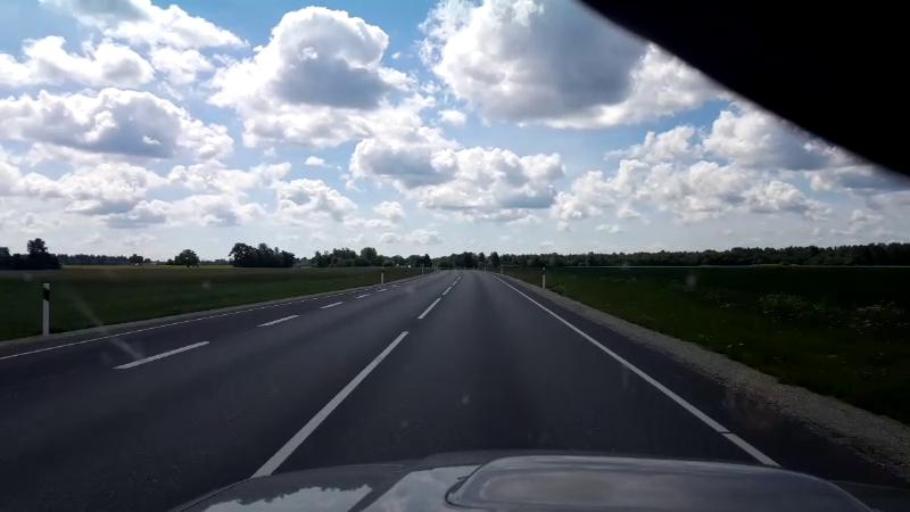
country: EE
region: Jaervamaa
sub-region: Jaerva-Jaani vald
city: Jarva-Jaani
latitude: 59.0814
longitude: 25.6839
